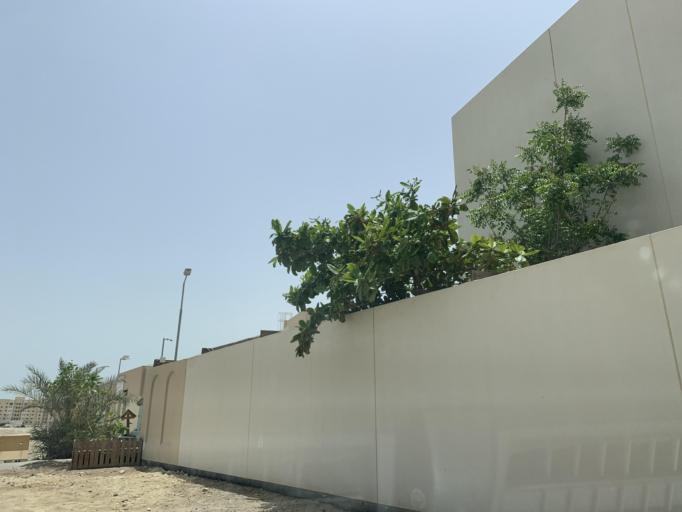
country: BH
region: Northern
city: Sitrah
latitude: 26.1468
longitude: 50.5919
